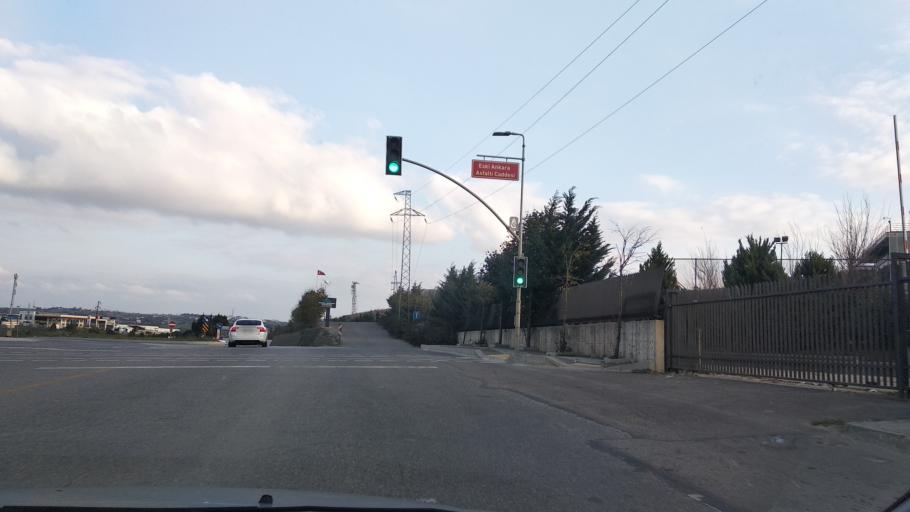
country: TR
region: Istanbul
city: Sultanbeyli
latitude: 40.9273
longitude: 29.3463
